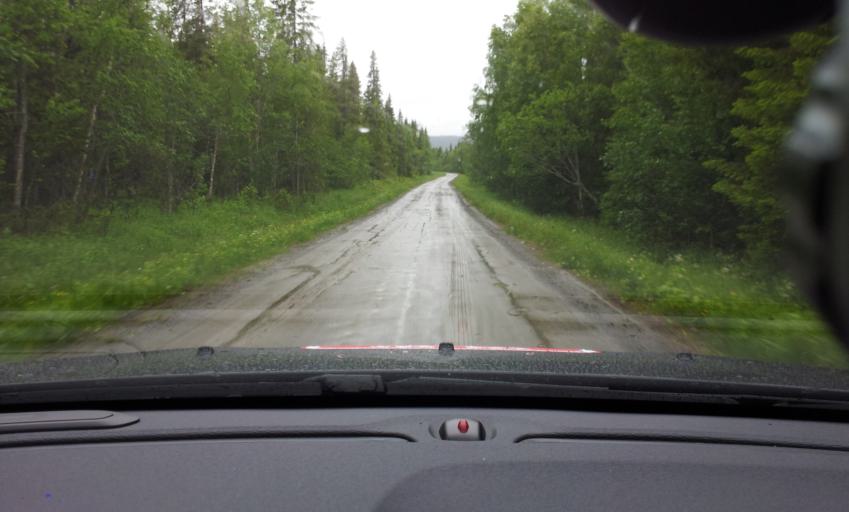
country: SE
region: Jaemtland
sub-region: Are Kommun
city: Are
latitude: 63.5081
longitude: 12.7082
